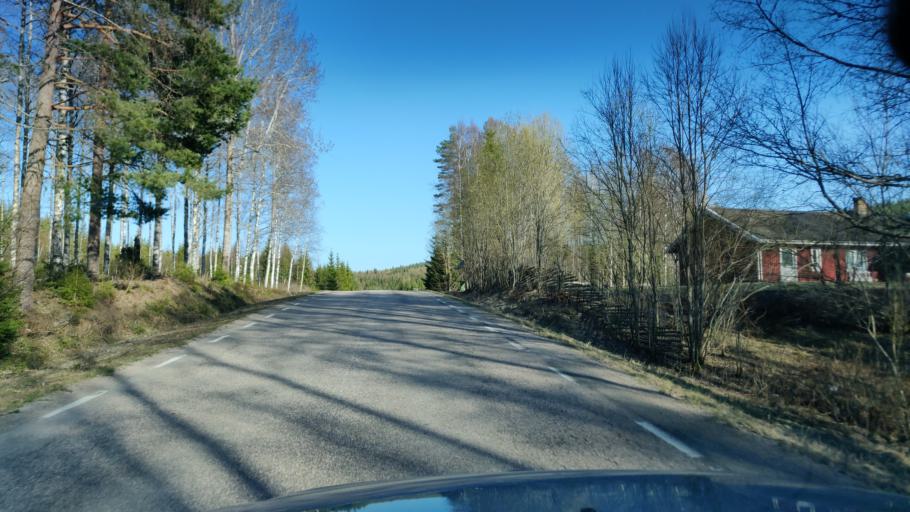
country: SE
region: Vaermland
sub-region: Munkfors Kommun
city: Munkfors
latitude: 59.9823
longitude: 13.3586
